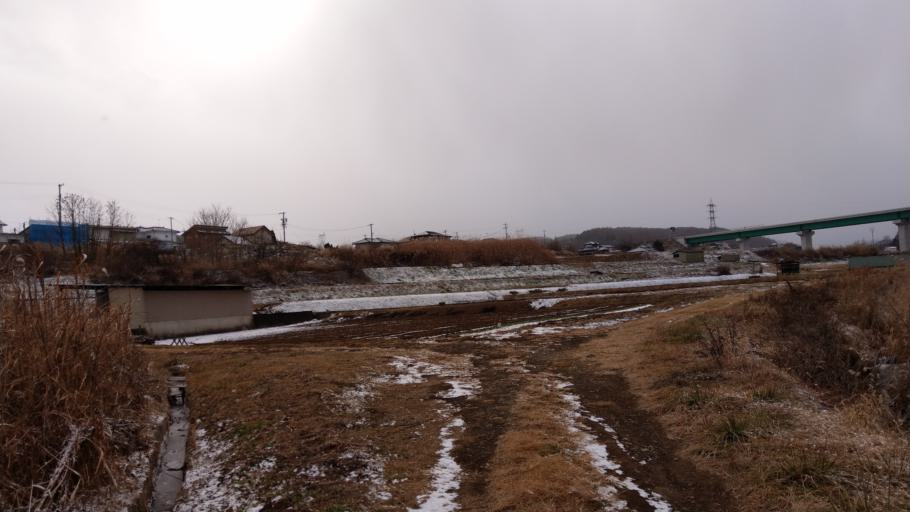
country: JP
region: Nagano
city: Saku
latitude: 36.1648
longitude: 138.4761
